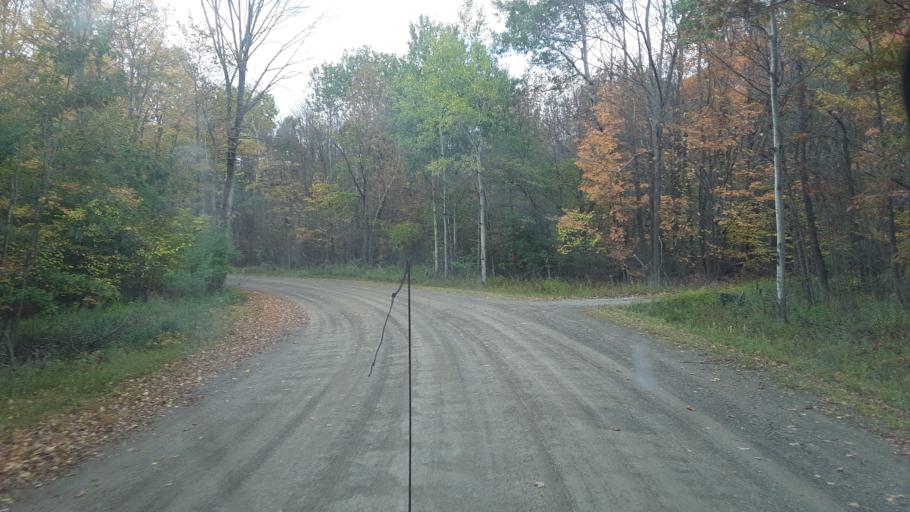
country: US
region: New York
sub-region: Allegany County
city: Alfred
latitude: 42.3904
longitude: -77.8684
